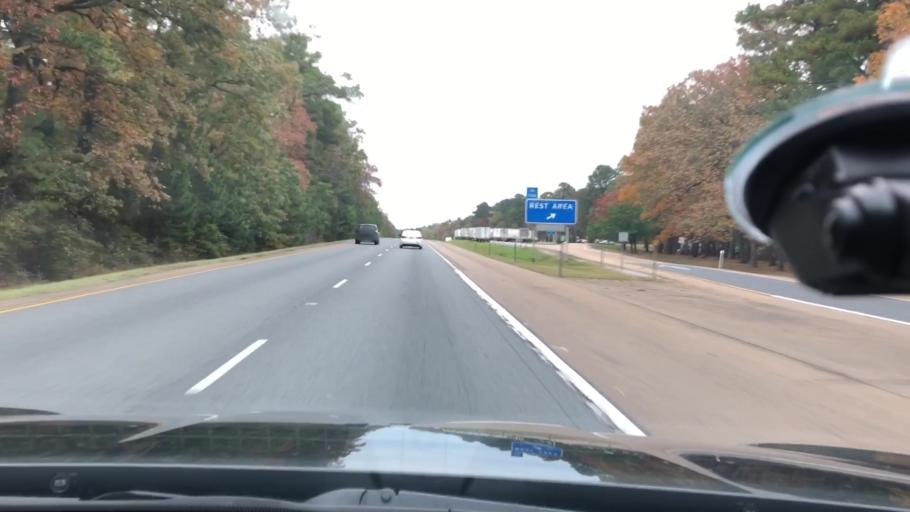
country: US
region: Arkansas
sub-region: Clark County
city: Gurdon
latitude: 33.9280
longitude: -93.2628
